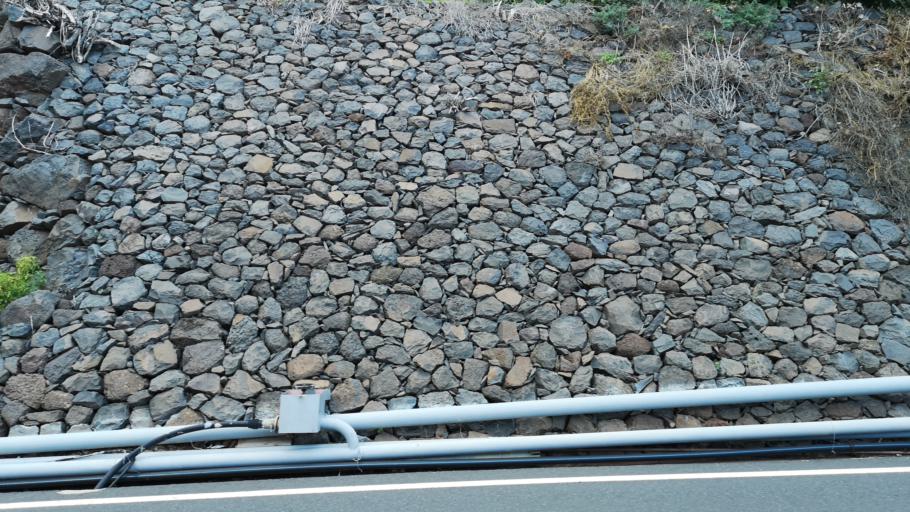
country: ES
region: Canary Islands
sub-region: Provincia de Santa Cruz de Tenerife
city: Agulo
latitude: 28.1864
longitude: -17.1976
